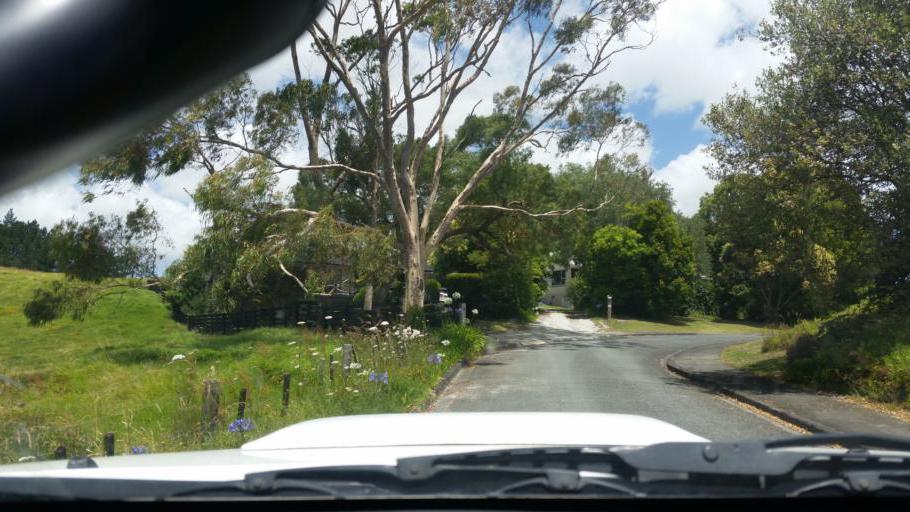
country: NZ
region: Northland
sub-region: Whangarei
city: Ruakaka
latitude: -36.0988
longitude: 174.2388
